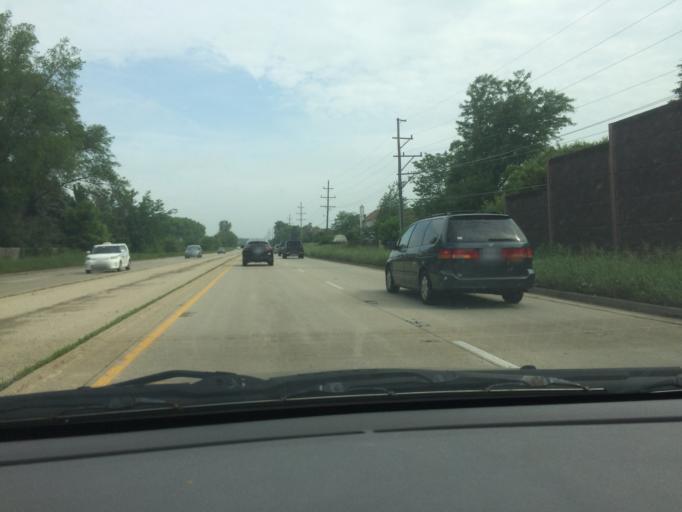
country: US
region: Illinois
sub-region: Cook County
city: Bartlett
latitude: 41.9647
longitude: -88.2062
